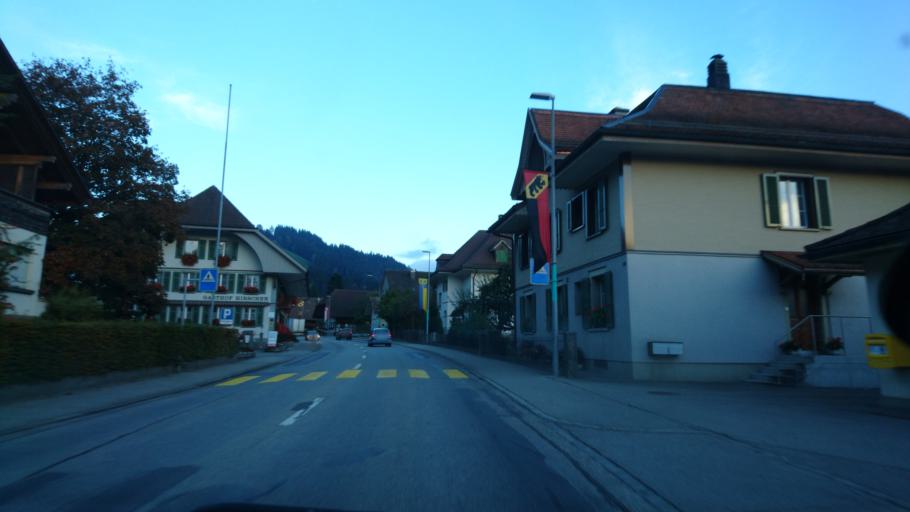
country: CH
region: Bern
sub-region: Emmental District
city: Trubschachen
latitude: 46.9227
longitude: 7.8407
